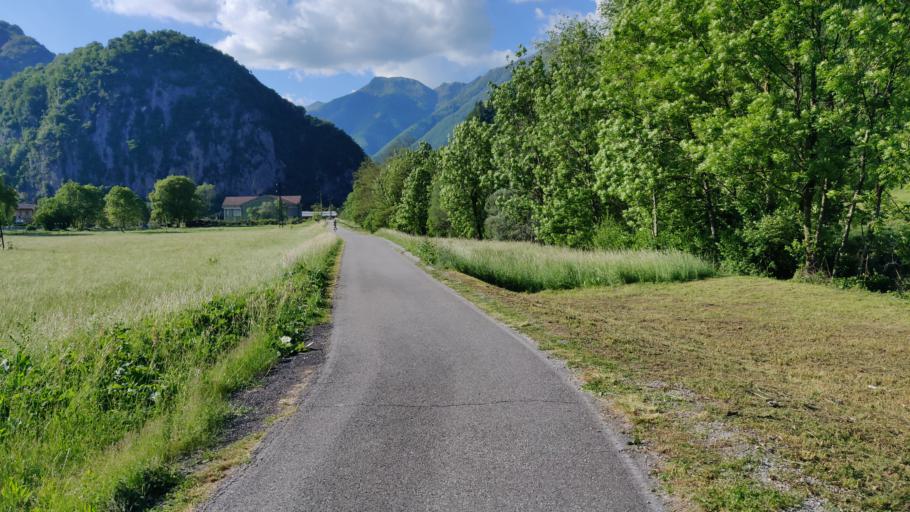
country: IT
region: Lombardy
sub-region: Provincia di Lecco
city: Pasturo
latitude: 45.9537
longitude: 9.4529
